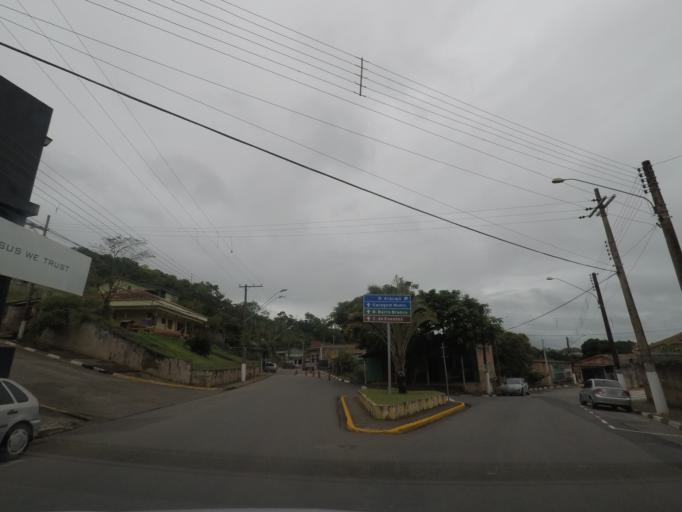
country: BR
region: Sao Paulo
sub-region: Cajati
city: Cajati
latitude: -24.7221
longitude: -48.1069
